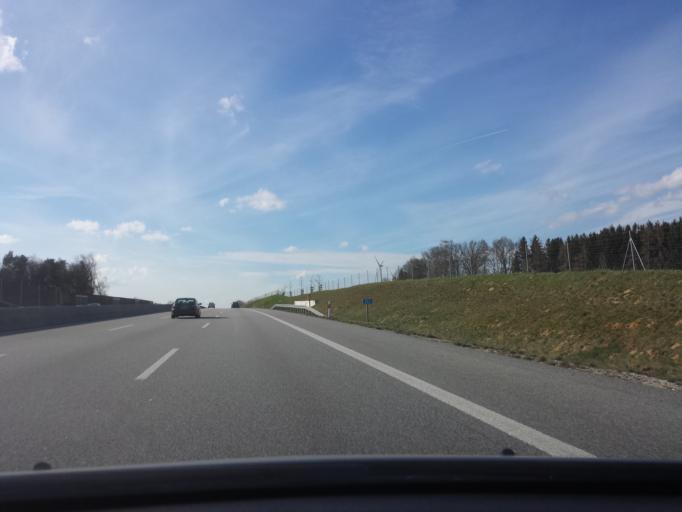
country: DE
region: Bavaria
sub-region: Upper Bavaria
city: Odelzhausen
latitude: 48.3182
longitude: 11.1909
